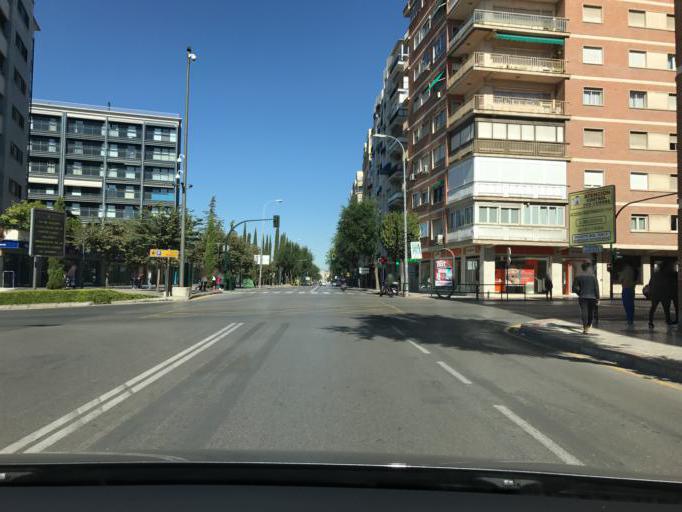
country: ES
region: Andalusia
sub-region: Provincia de Granada
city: Granada
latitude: 37.1692
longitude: -3.6069
